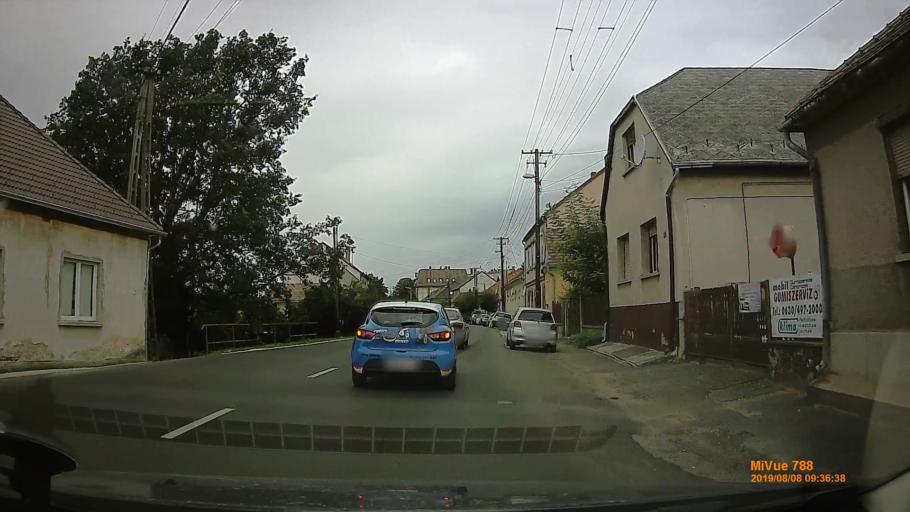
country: HU
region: Vas
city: Vasvar
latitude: 47.0474
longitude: 16.8050
